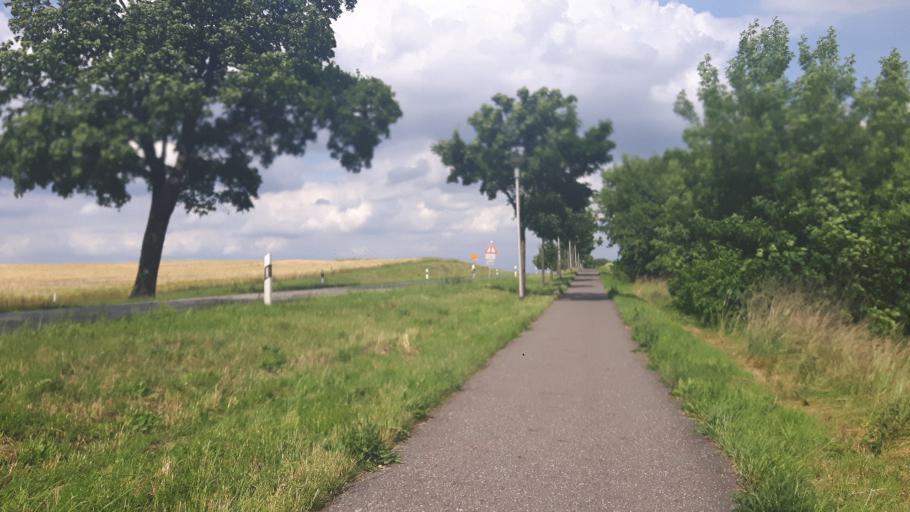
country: DE
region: Berlin
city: Buch
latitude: 52.6307
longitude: 13.5474
